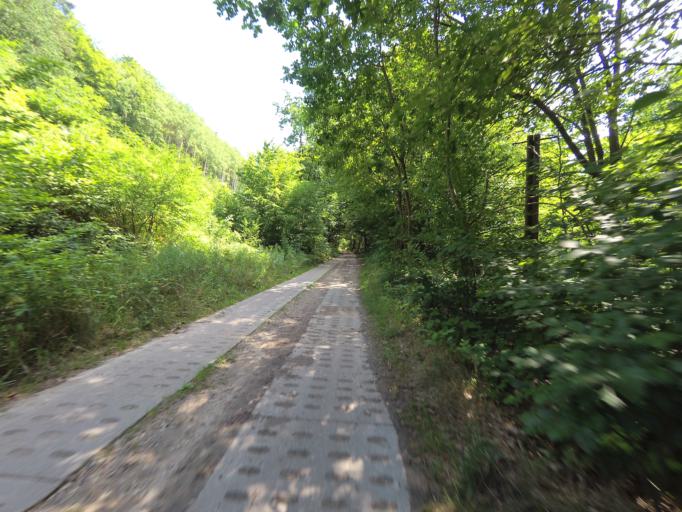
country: PL
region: Pomeranian Voivodeship
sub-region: Gdynia
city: Wielki Kack
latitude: 54.4890
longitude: 18.5015
